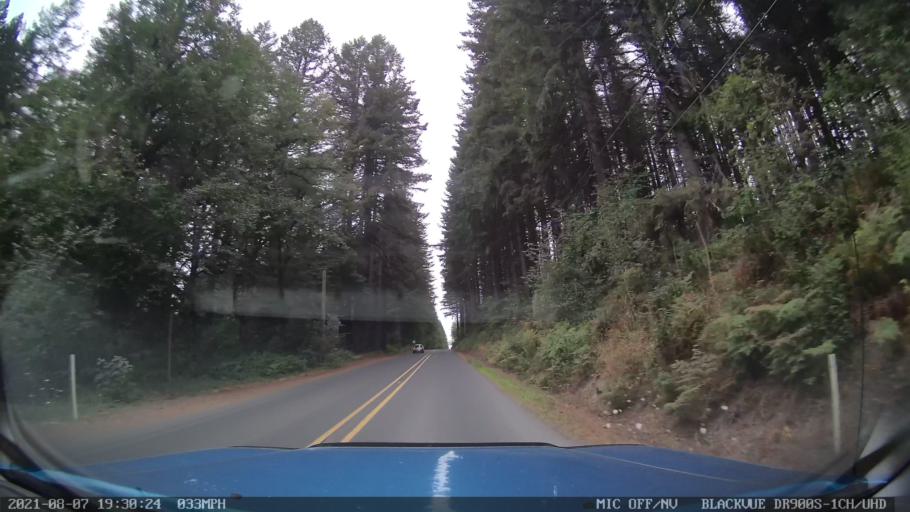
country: US
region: Oregon
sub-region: Linn County
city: Lyons
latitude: 44.8848
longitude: -122.6205
